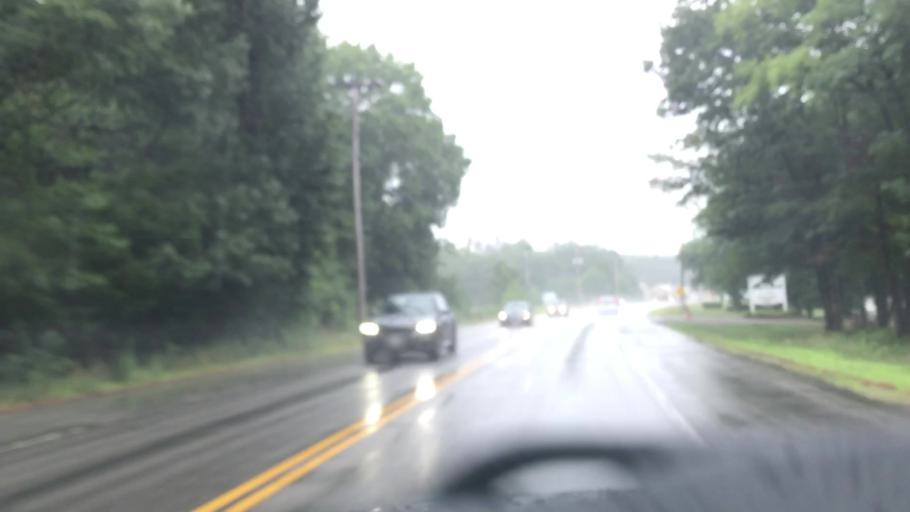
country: US
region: Maine
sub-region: York County
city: Wells Beach Station
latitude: 43.3186
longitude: -70.6493
